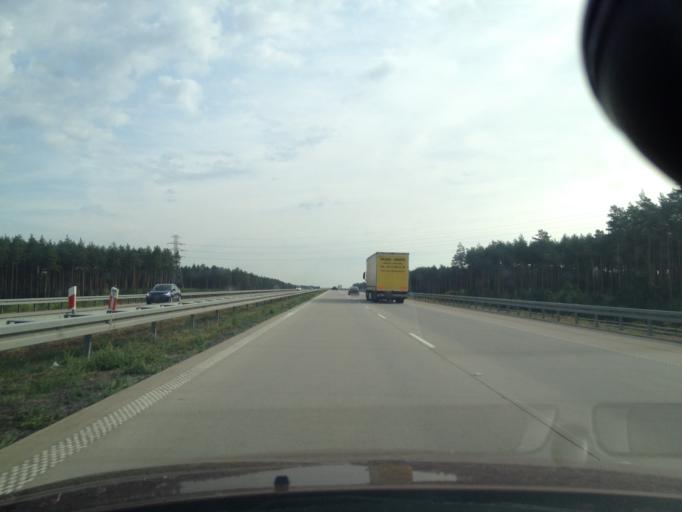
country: PL
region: Lower Silesian Voivodeship
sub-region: Powiat boleslawiecki
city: Boleslawiec
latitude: 51.2910
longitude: 15.4898
